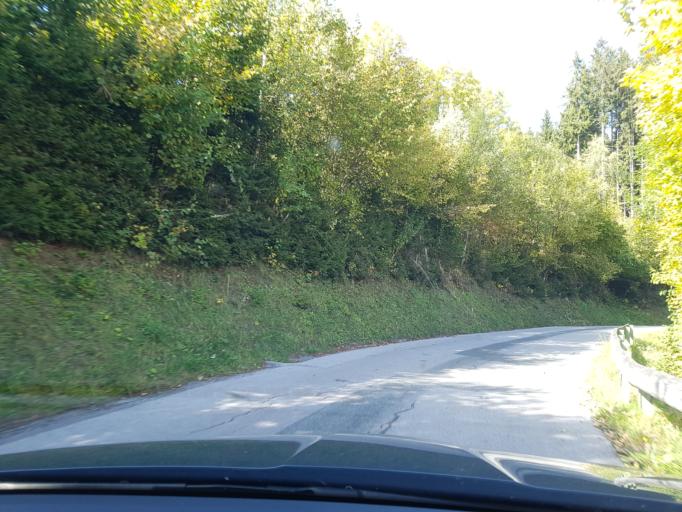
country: AT
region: Salzburg
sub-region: Politischer Bezirk Sankt Johann im Pongau
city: Radstadt
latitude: 47.3893
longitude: 13.4748
